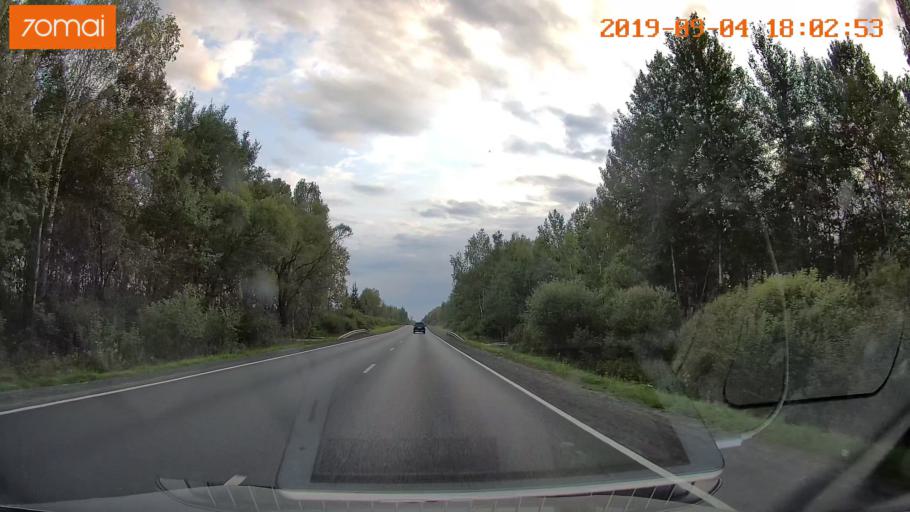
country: RU
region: Moskovskaya
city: Il'inskiy Pogost
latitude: 55.4693
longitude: 38.8590
